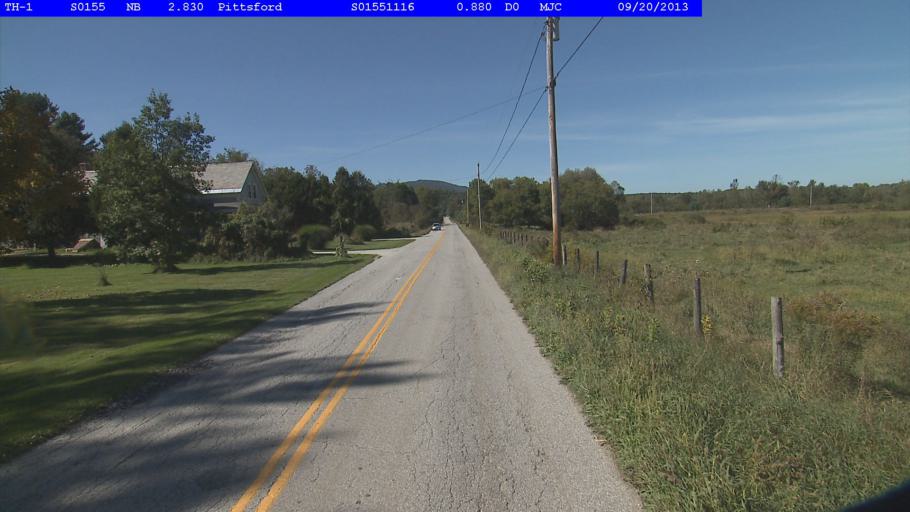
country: US
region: Vermont
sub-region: Rutland County
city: Brandon
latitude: 43.7040
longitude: -73.0470
